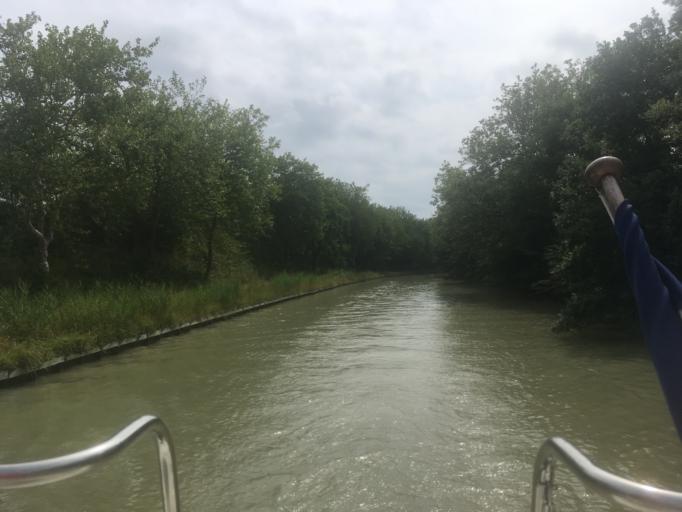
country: FR
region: Languedoc-Roussillon
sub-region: Departement de l'Aude
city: Villepinte
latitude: 43.2765
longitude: 2.0673
